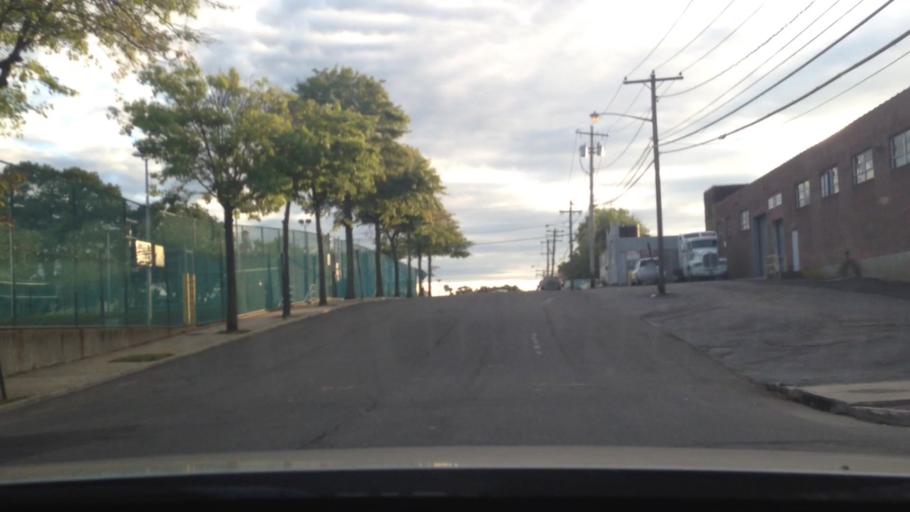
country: US
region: New York
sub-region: Nassau County
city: Garden City Park
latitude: 40.7379
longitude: -73.6592
